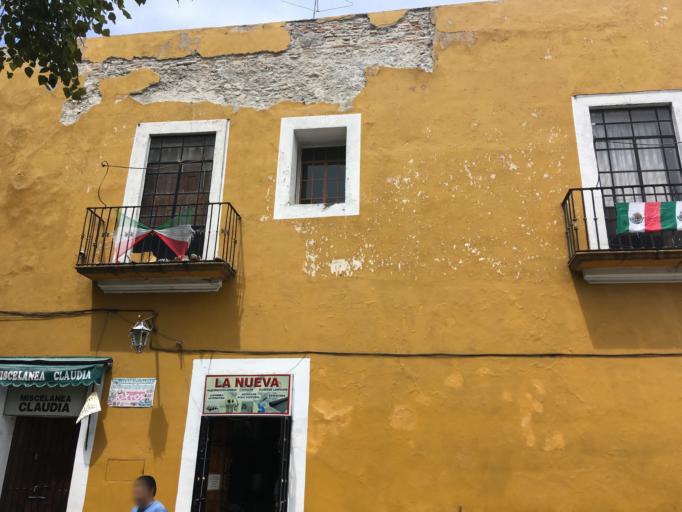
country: MX
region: Puebla
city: Puebla
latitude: 19.0457
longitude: -98.1917
